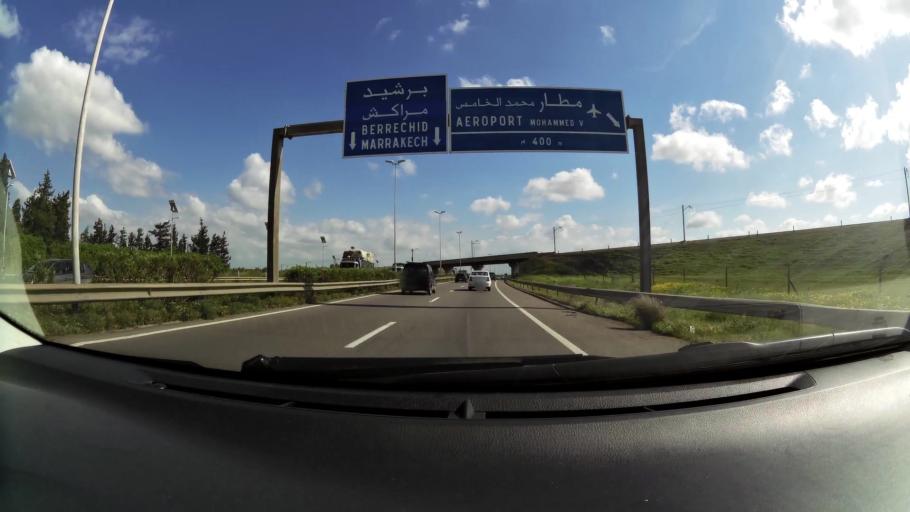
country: MA
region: Chaouia-Ouardigha
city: Nouaseur
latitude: 33.3981
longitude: -7.6209
